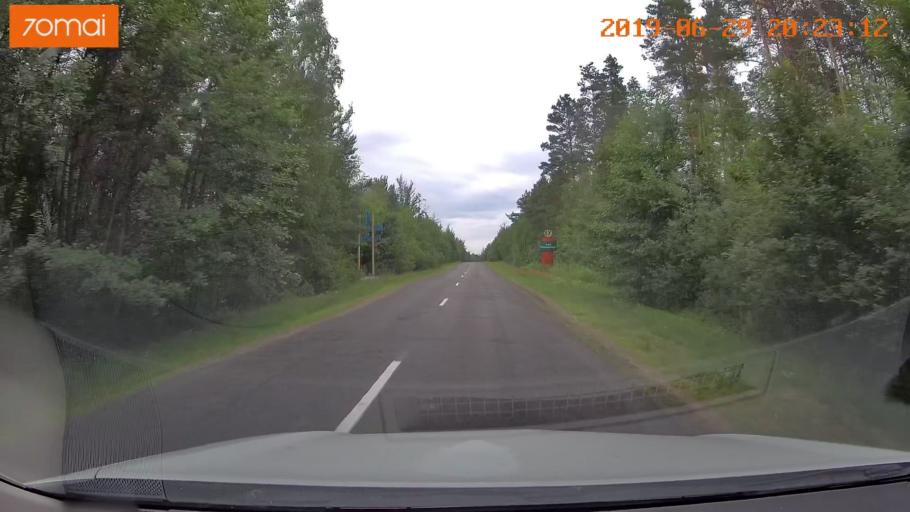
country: BY
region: Brest
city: Asnyezhytsy
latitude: 52.4415
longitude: 26.2592
